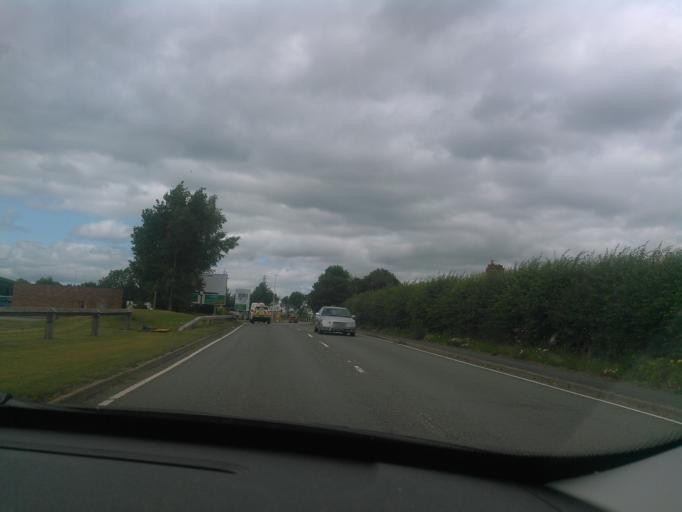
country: GB
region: England
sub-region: Shropshire
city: Berrington
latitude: 52.6907
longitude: -2.7074
